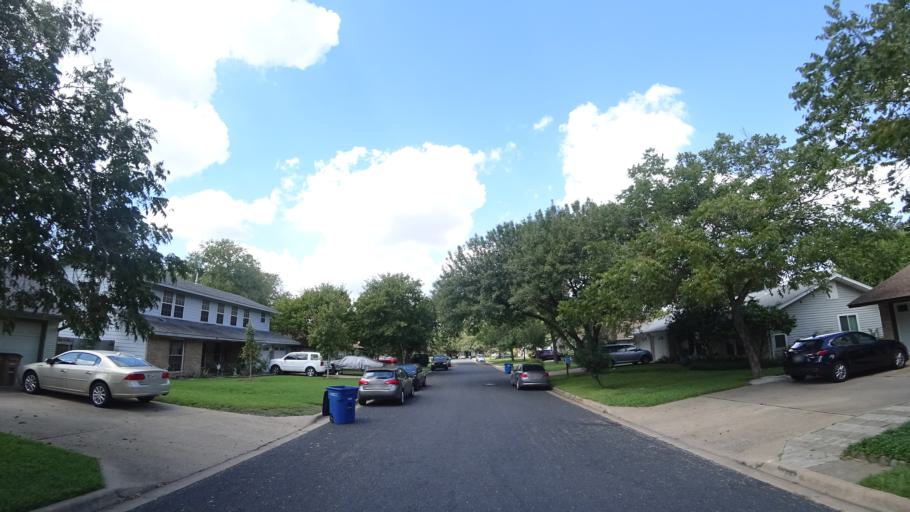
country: US
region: Texas
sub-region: Travis County
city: Austin
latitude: 30.3577
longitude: -97.7261
